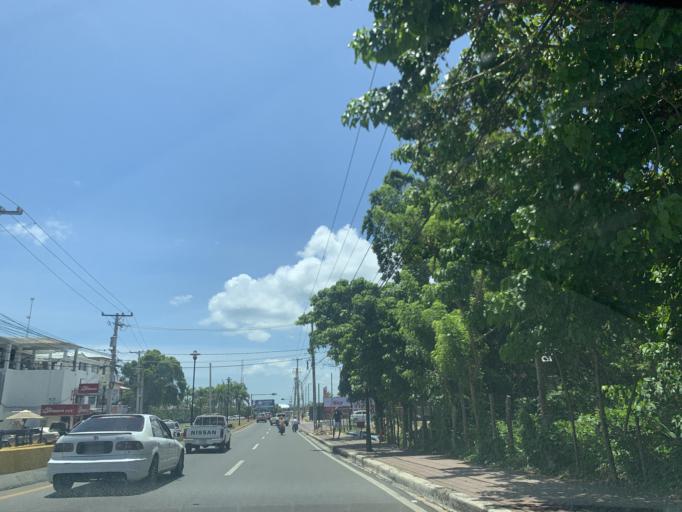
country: DO
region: Puerto Plata
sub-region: Puerto Plata
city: Puerto Plata
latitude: 19.7830
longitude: -70.6752
